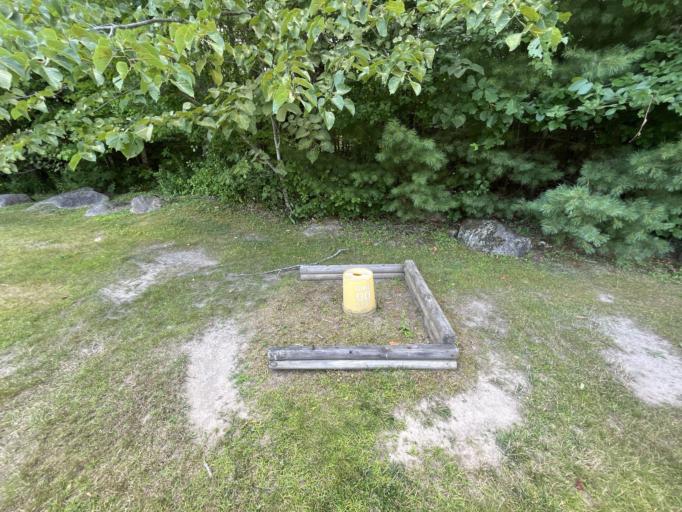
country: US
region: New Hampshire
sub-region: Grafton County
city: Hanover
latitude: 43.6789
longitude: -72.2616
